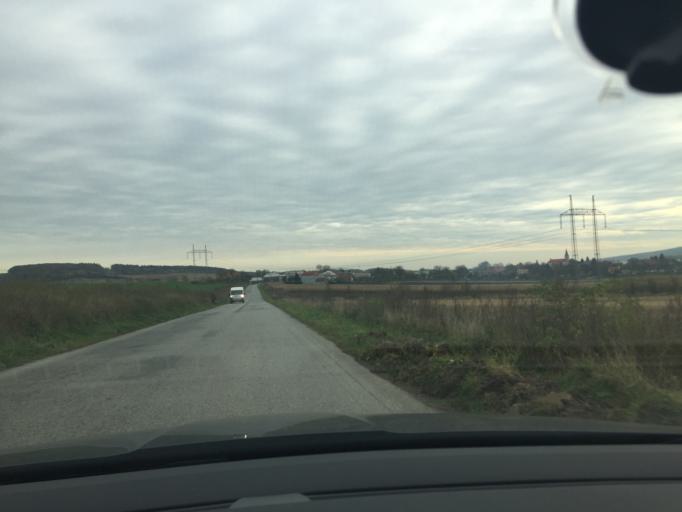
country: SK
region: Kosicky
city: Kosice
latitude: 48.8230
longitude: 21.3222
